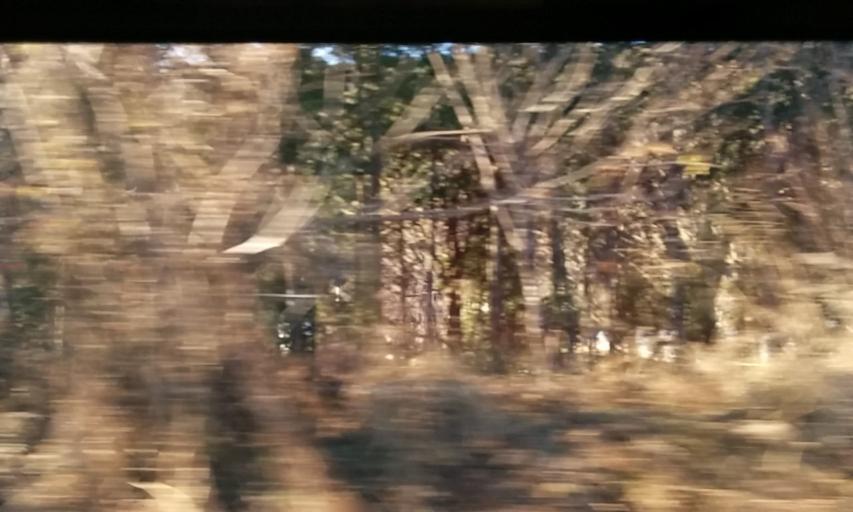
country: JP
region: Nagano
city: Ina
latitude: 35.8795
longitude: 137.7538
